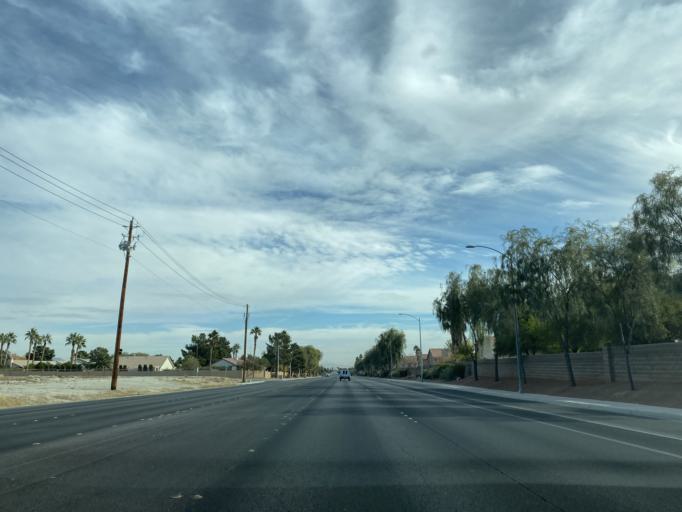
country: US
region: Nevada
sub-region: Clark County
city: Las Vegas
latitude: 36.2464
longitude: -115.2228
